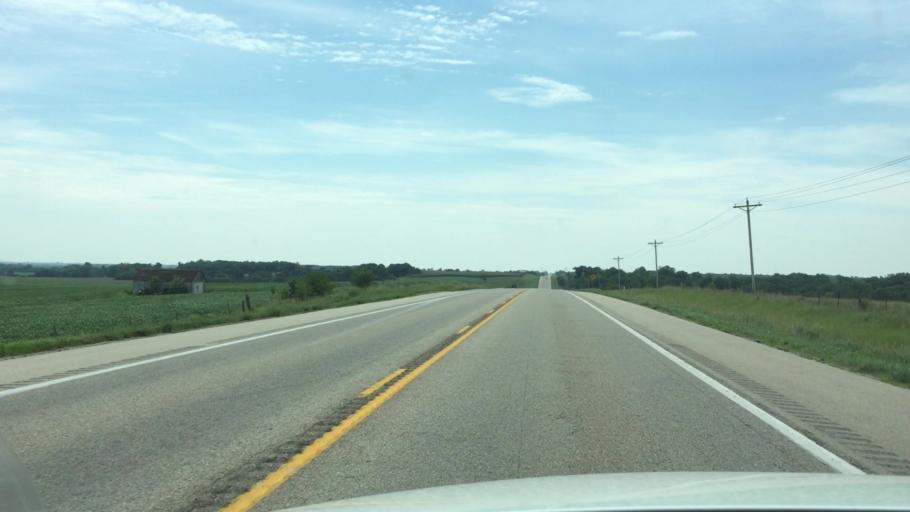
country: US
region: Kansas
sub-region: Nemaha County
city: Sabetha
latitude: 39.7451
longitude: -95.7297
